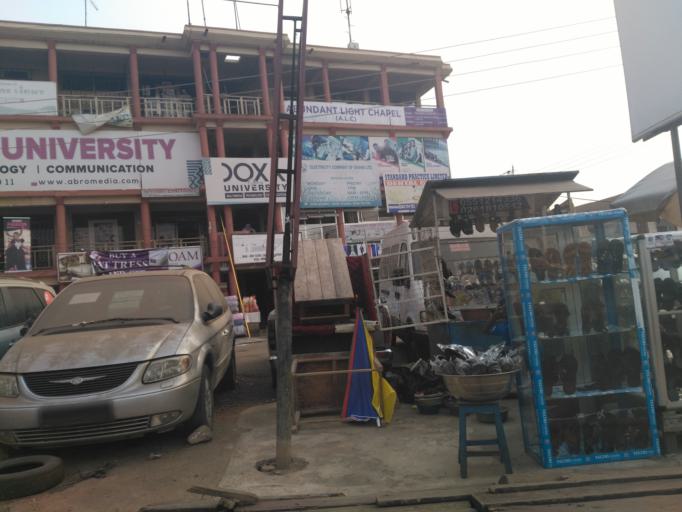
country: GH
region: Ashanti
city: Kumasi
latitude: 6.6892
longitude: -1.6136
